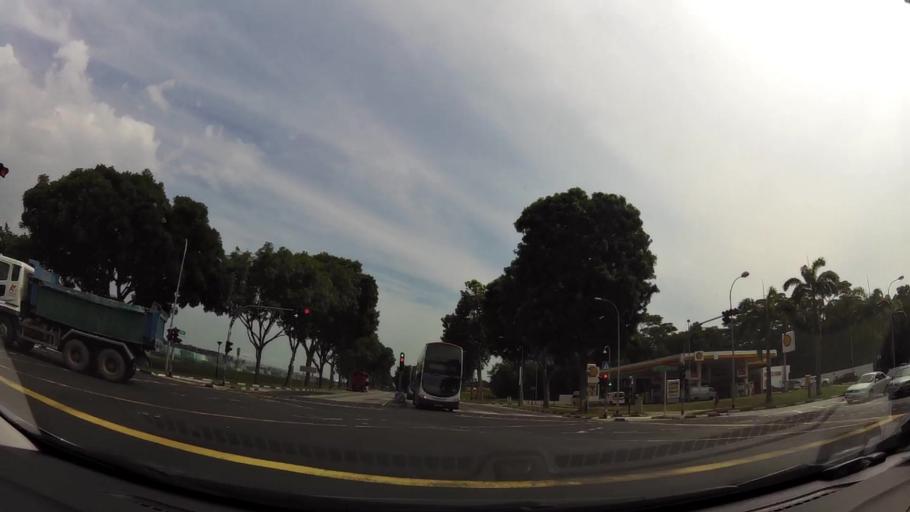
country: MY
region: Johor
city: Kampung Pasir Gudang Baru
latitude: 1.3656
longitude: 103.9666
